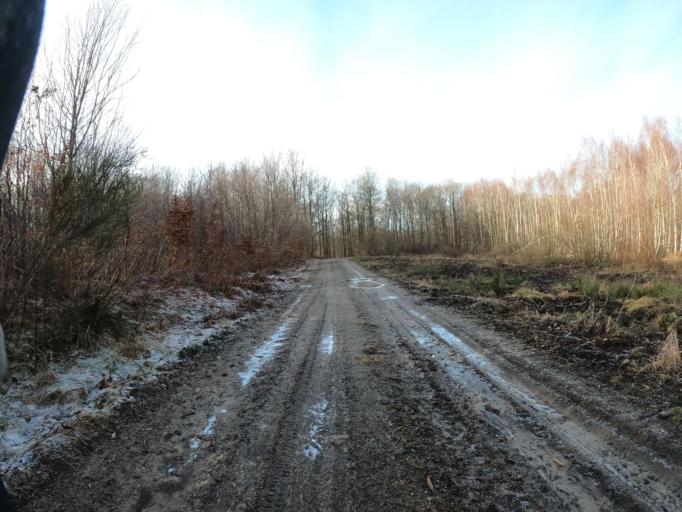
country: PL
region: West Pomeranian Voivodeship
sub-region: Powiat koszalinski
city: Polanow
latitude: 54.1575
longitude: 16.7577
